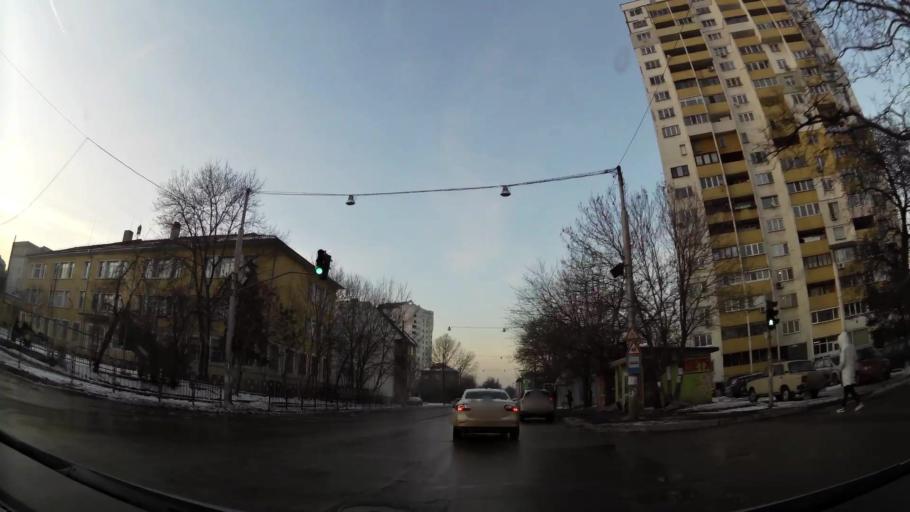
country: BG
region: Sofia-Capital
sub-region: Stolichna Obshtina
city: Sofia
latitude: 42.6898
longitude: 23.3704
